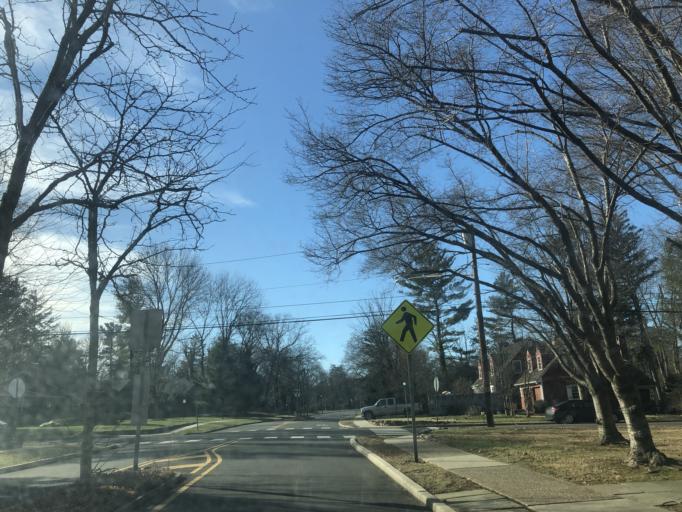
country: US
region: New Jersey
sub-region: Mercer County
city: Princeton
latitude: 40.3522
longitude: -74.6395
